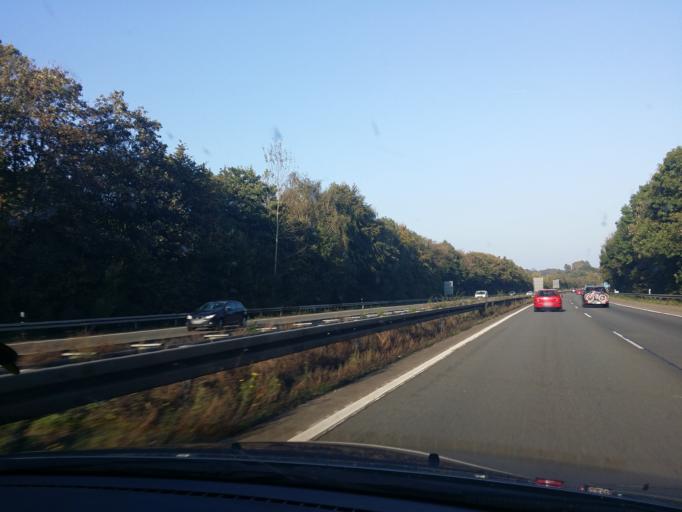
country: DE
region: Lower Saxony
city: Hasbergen
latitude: 52.2392
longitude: 7.8888
